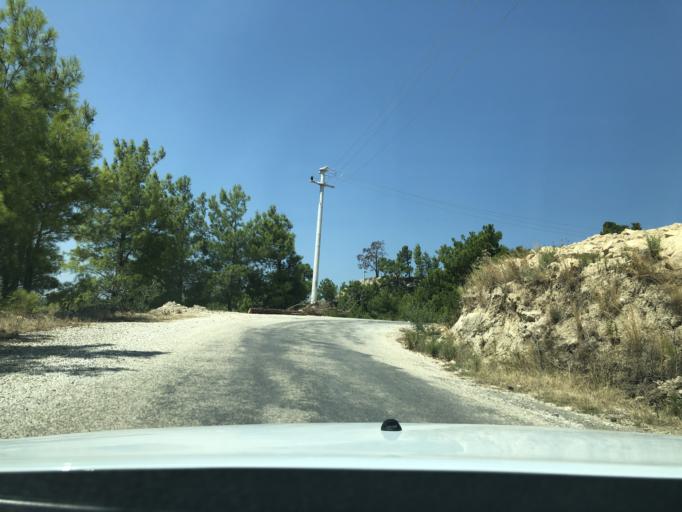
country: TR
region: Antalya
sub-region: Manavgat
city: Manavgat
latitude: 36.8693
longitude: 31.5560
